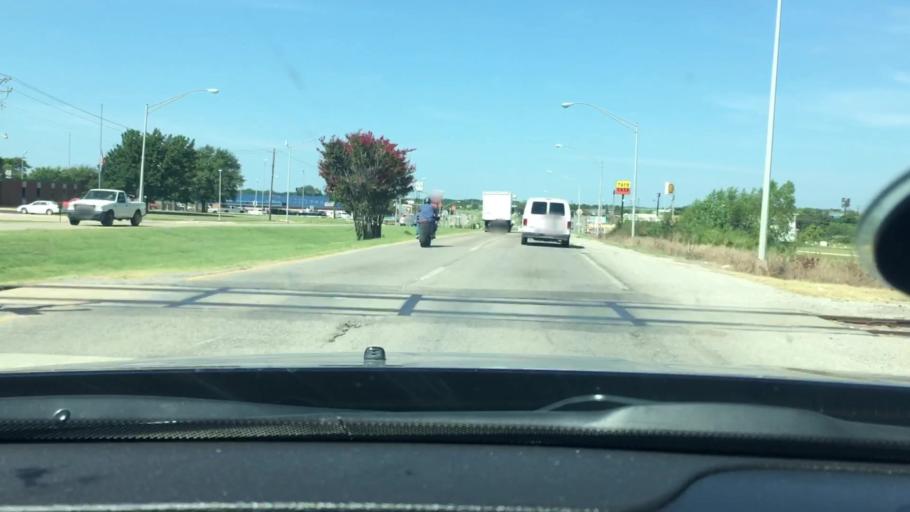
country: US
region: Oklahoma
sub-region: Carter County
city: Ardmore
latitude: 34.1730
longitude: -97.1567
